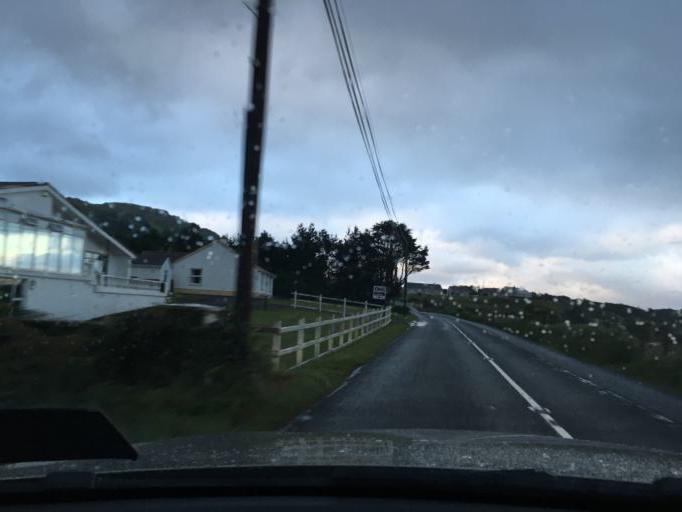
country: IE
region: Ulster
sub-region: County Donegal
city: Killybegs
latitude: 54.6344
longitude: -8.4984
